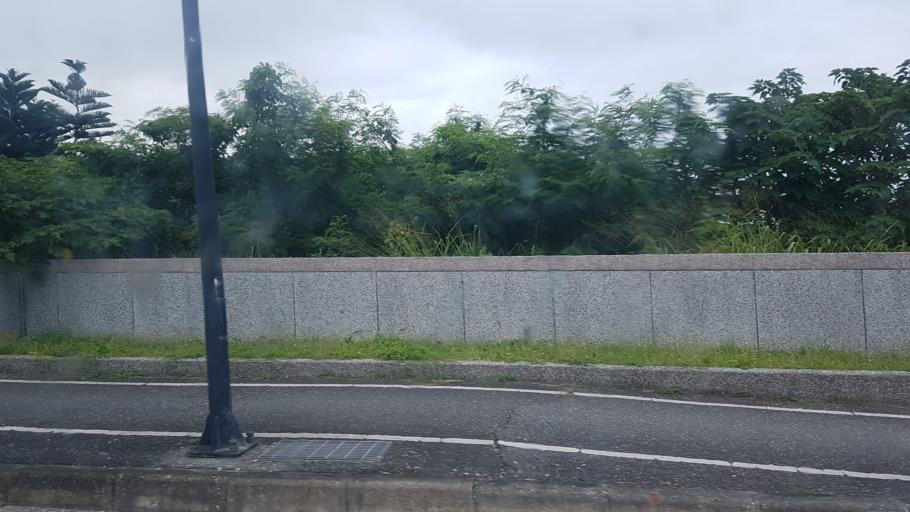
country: TW
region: Taiwan
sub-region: Hualien
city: Hualian
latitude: 24.0024
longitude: 121.6403
